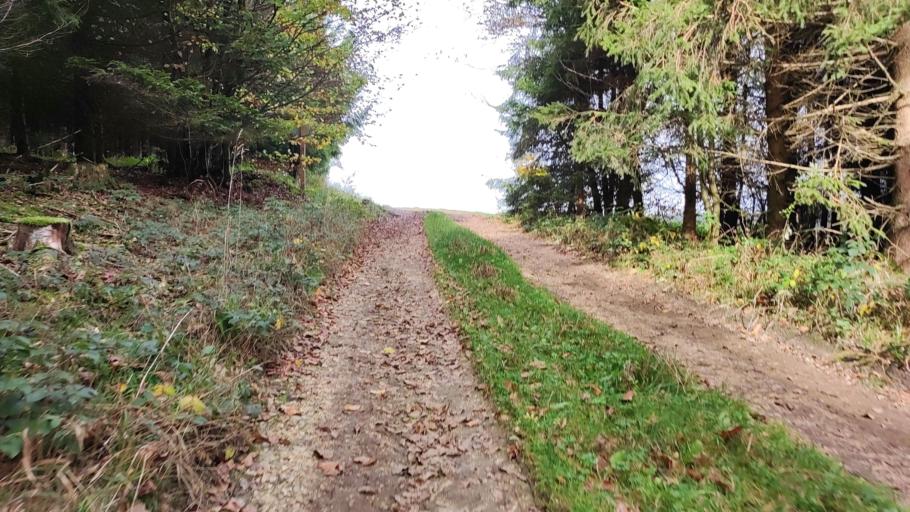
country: DE
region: Bavaria
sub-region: Swabia
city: Ziemetshausen
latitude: 48.2776
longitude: 10.5635
